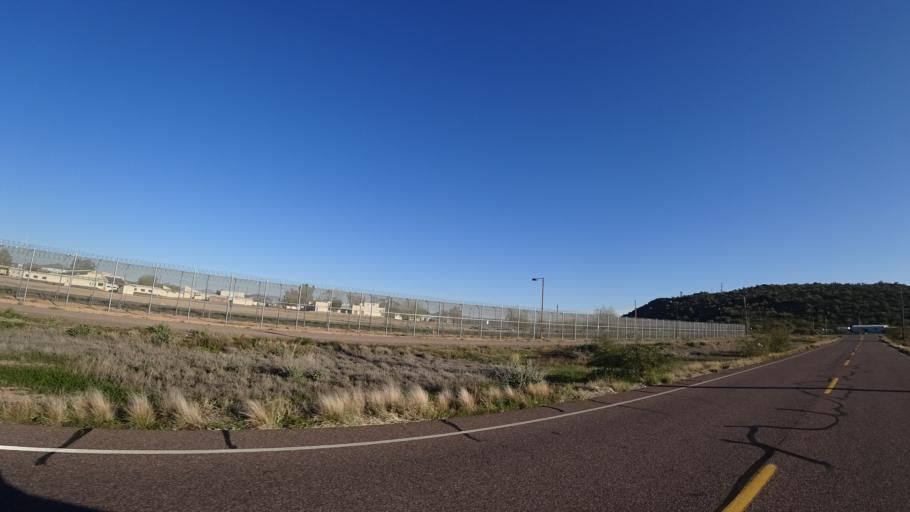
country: US
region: Arizona
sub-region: Maricopa County
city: Anthem
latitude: 33.7031
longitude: -112.1219
